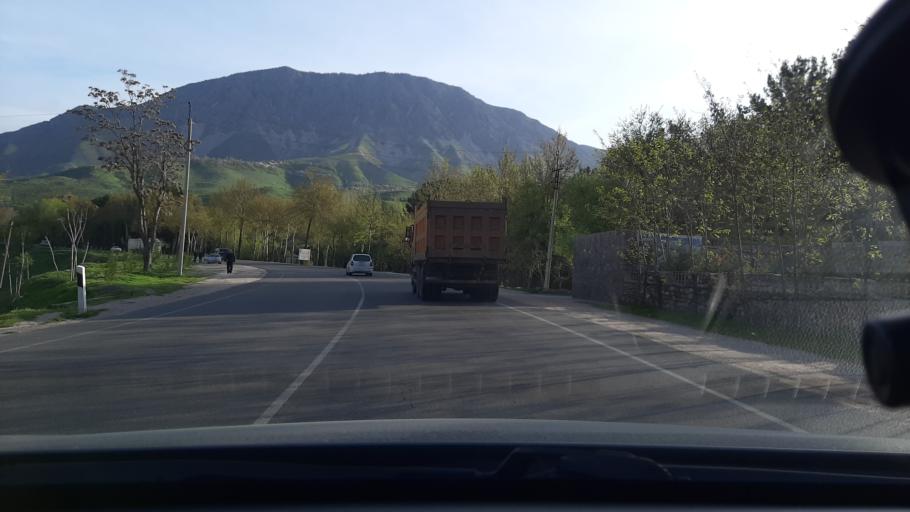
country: TJ
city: Varzob
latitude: 38.6791
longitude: 68.7906
